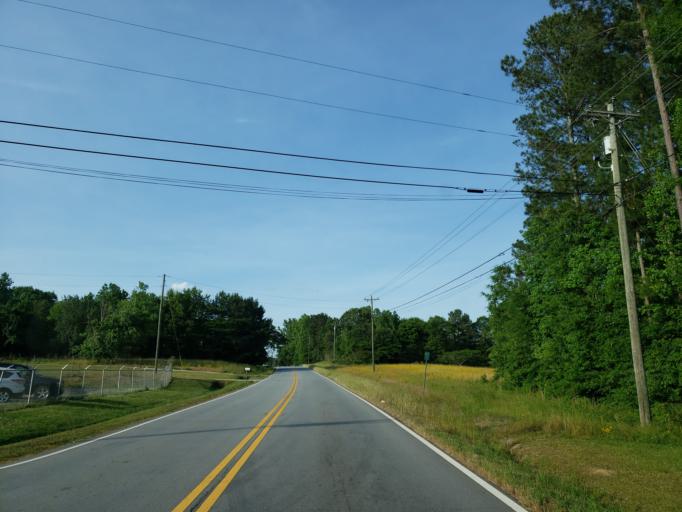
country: US
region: Georgia
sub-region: Carroll County
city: Bowdon
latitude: 33.5122
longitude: -85.2646
